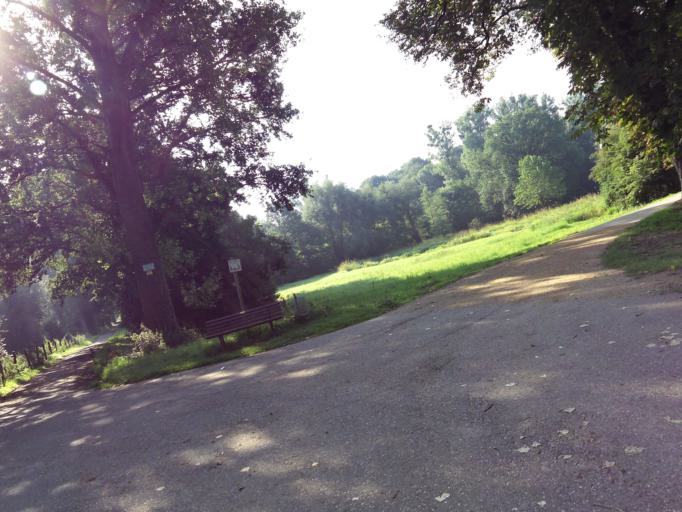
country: DE
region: North Rhine-Westphalia
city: Geilenkirchen
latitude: 50.9720
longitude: 6.1350
